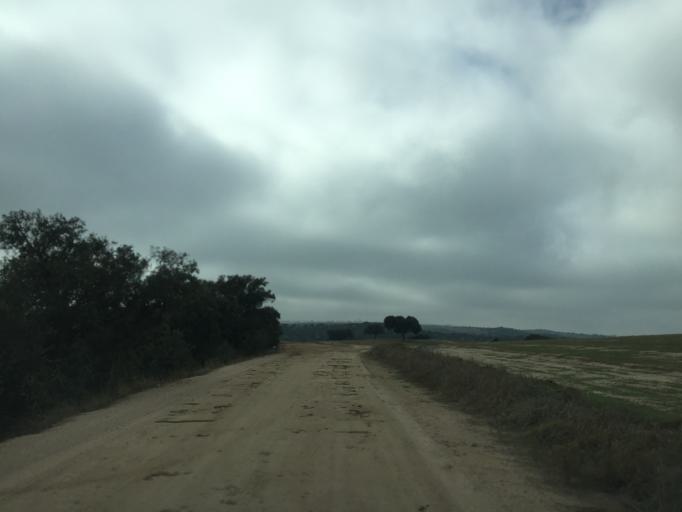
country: PT
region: Portalegre
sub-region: Fronteira
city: Fronteira
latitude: 39.0722
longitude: -7.6113
